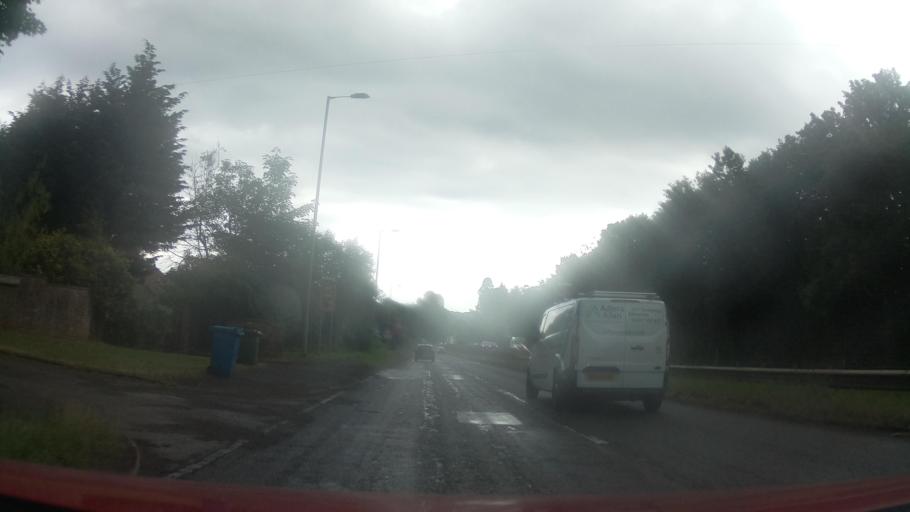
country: GB
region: England
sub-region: Dudley
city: Kingswinford
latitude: 52.5523
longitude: -2.1721
